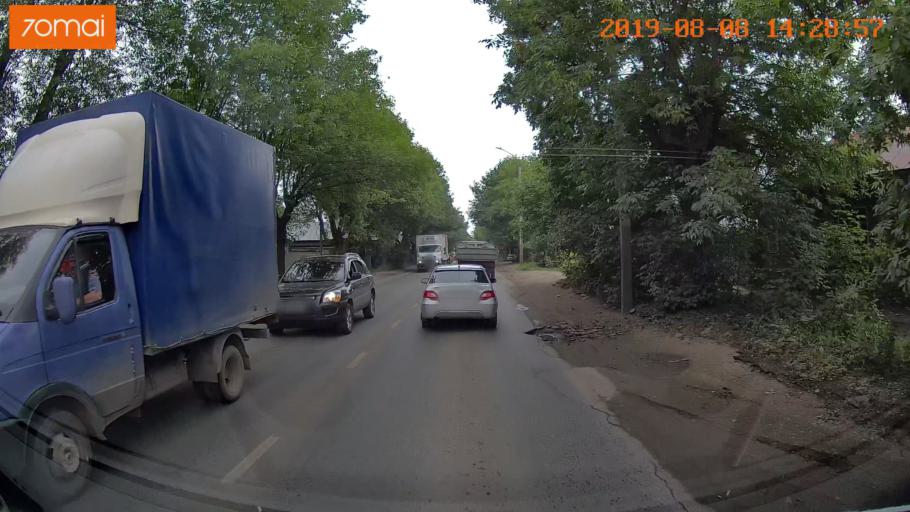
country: RU
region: Ivanovo
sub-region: Gorod Ivanovo
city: Ivanovo
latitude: 56.9966
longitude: 40.9509
